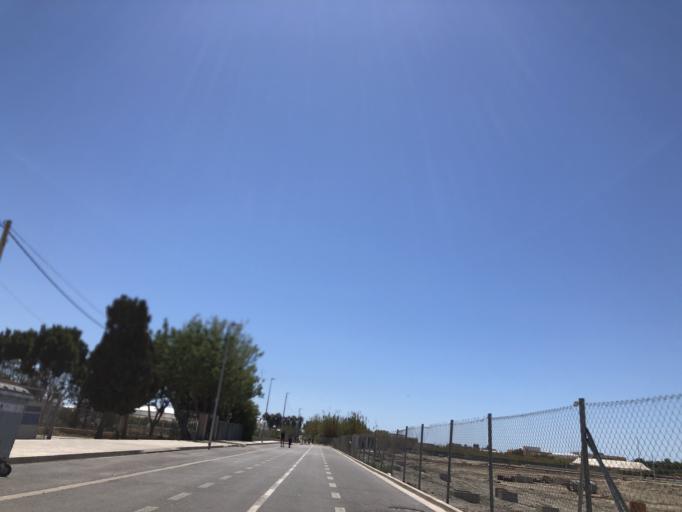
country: ES
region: Andalusia
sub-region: Provincia de Almeria
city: Almeria
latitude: 36.8367
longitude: -2.4048
